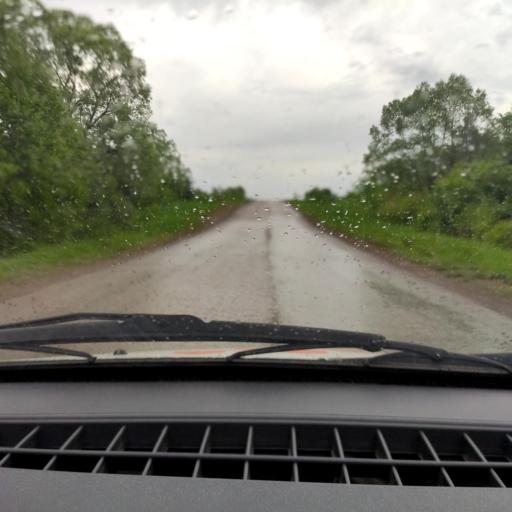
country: RU
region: Bashkortostan
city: Urman
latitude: 54.8542
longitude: 56.8234
